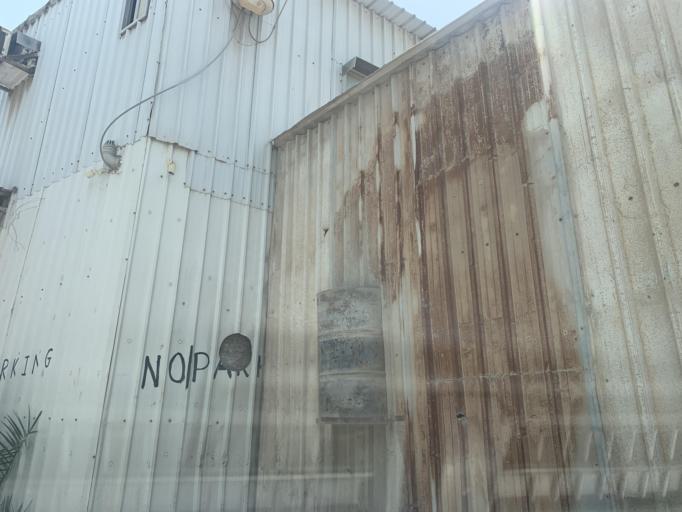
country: BH
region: Central Governorate
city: Madinat Hamad
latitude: 26.1413
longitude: 50.4891
